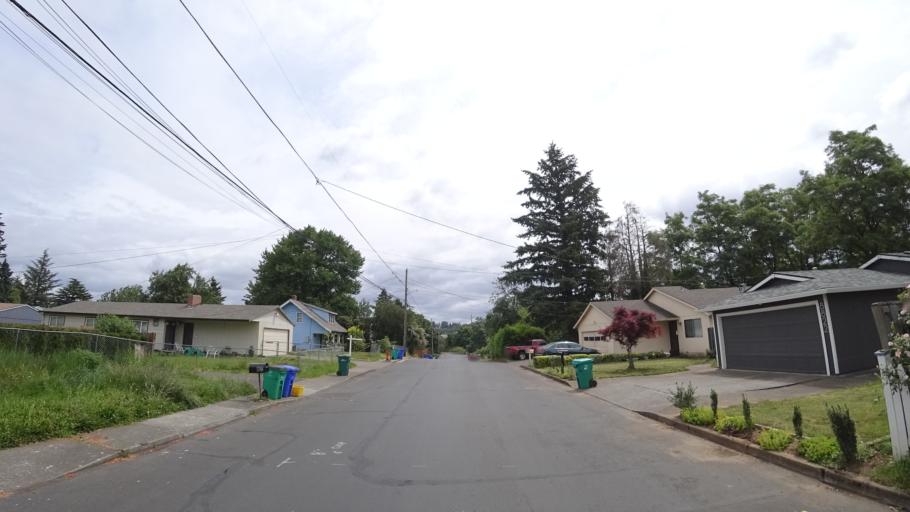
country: US
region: Oregon
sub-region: Multnomah County
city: Lents
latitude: 45.4703
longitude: -122.5722
